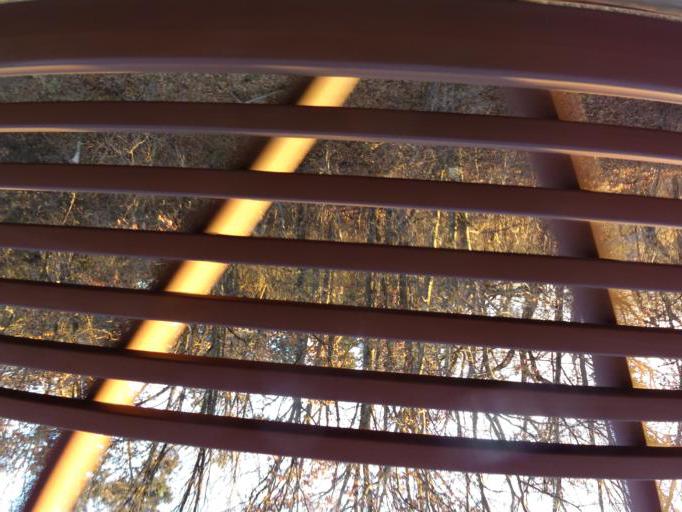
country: US
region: Minnesota
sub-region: Washington County
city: Grant
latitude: 45.0802
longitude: -92.8964
